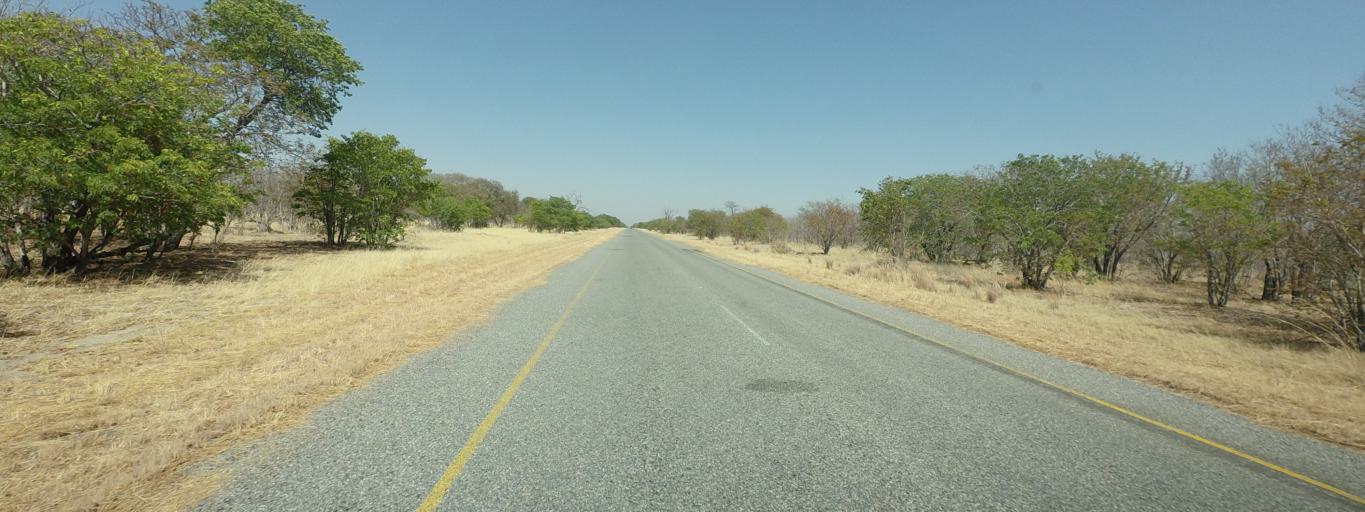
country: BW
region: North West
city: Kasane
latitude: -17.9218
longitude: 24.9820
